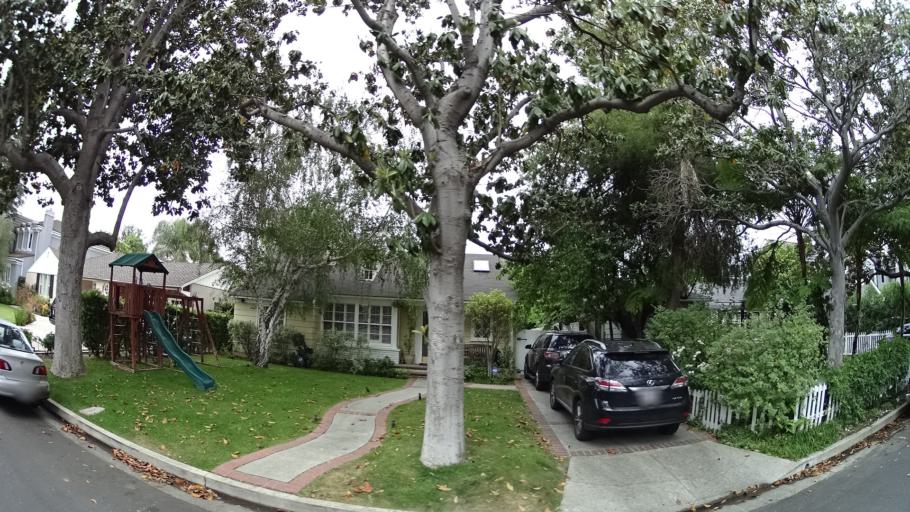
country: US
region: California
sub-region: Los Angeles County
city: North Hollywood
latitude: 34.1495
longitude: -118.4084
